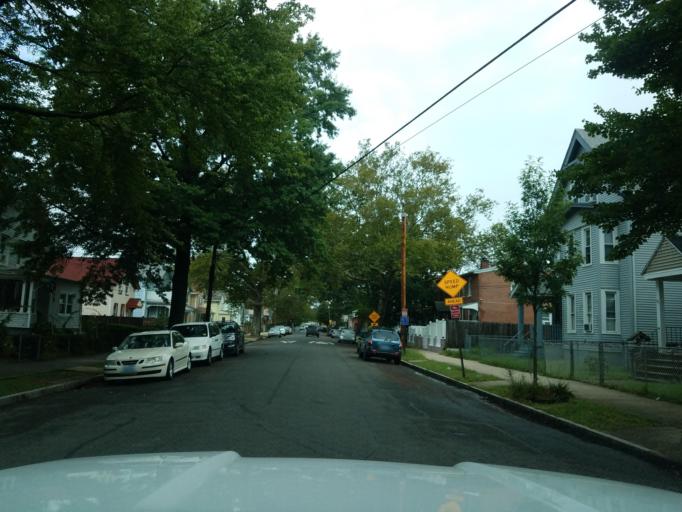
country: US
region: Connecticut
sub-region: New Haven County
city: New Haven
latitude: 41.2874
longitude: -72.9328
